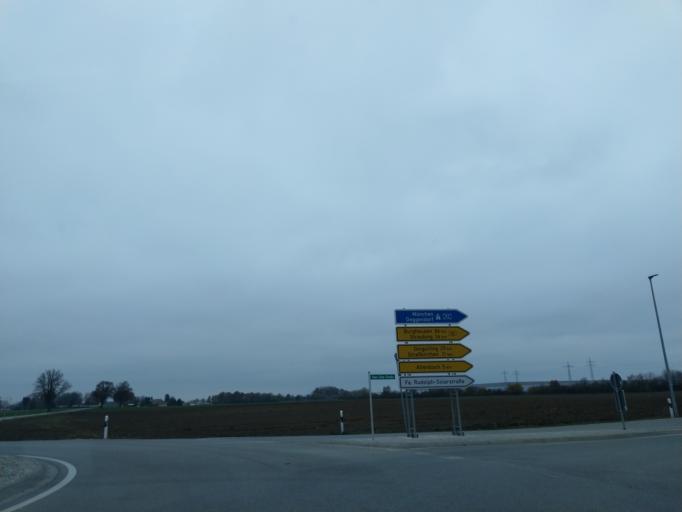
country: DE
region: Bavaria
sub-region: Lower Bavaria
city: Wallersdorf
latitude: 48.7483
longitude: 12.7583
